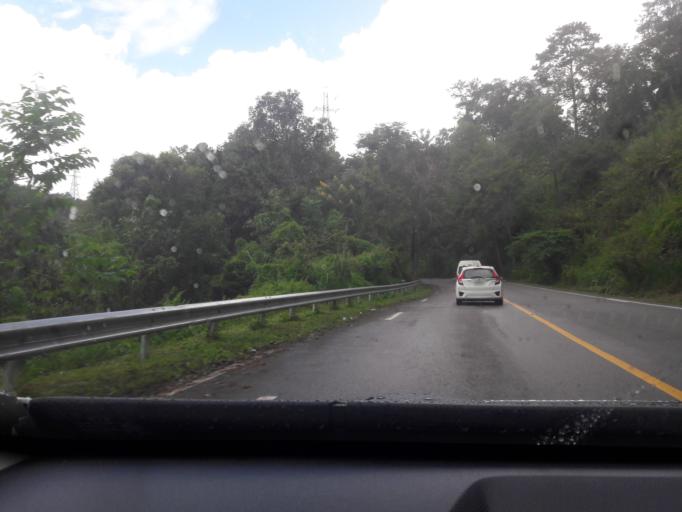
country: TH
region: Mae Hong Son
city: Mae Hi
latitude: 19.2308
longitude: 98.6698
